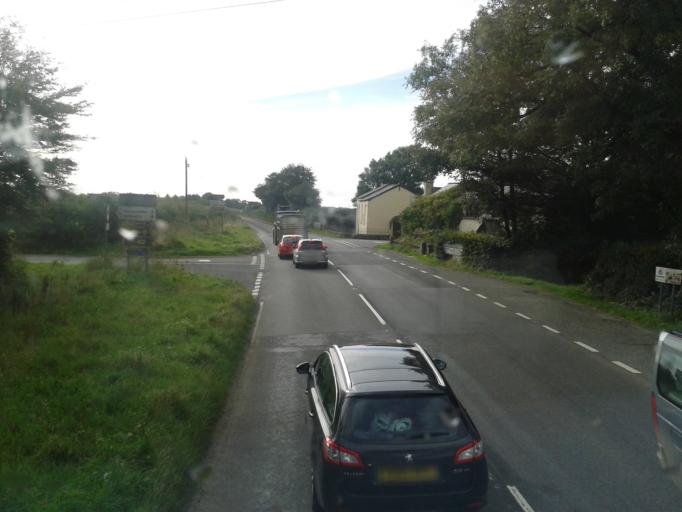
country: GB
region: England
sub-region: Devon
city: Holsworthy
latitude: 50.8143
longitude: -4.3110
